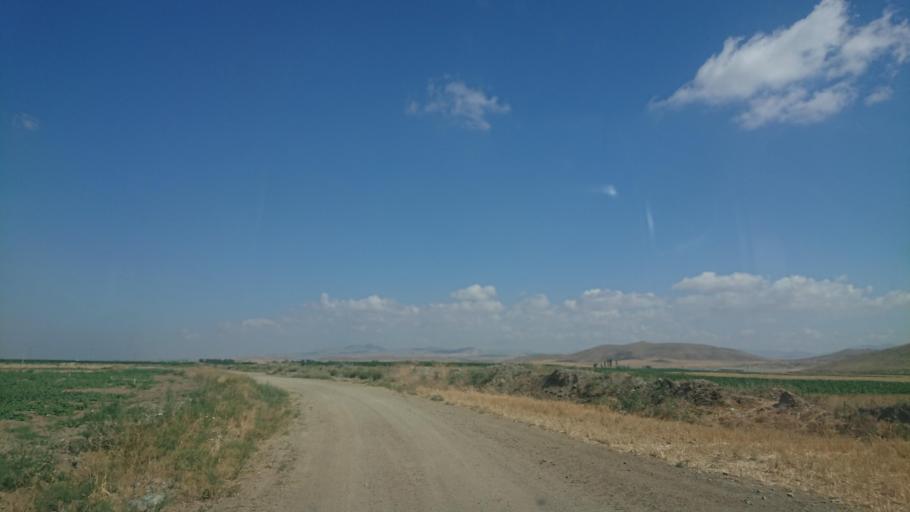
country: TR
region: Aksaray
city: Sariyahsi
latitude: 38.9812
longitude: 33.9090
